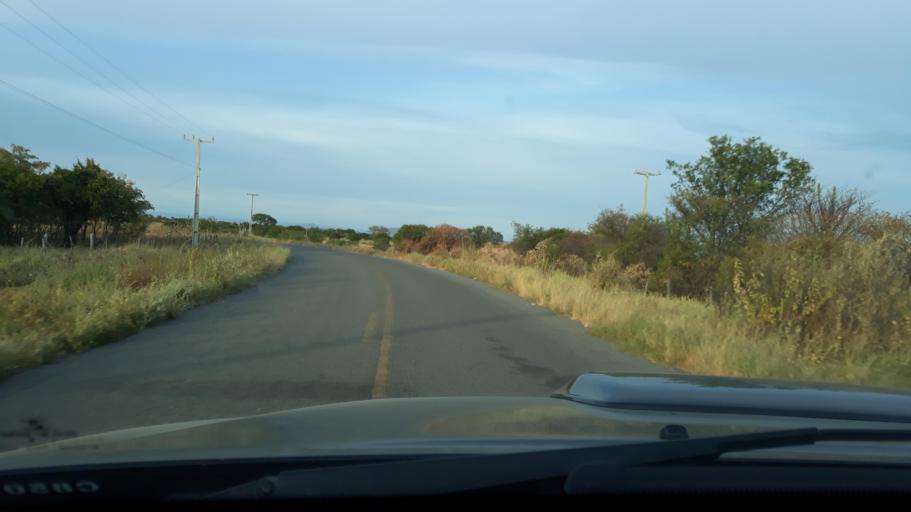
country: BR
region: Bahia
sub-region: Guanambi
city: Guanambi
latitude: -13.9474
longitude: -42.8535
